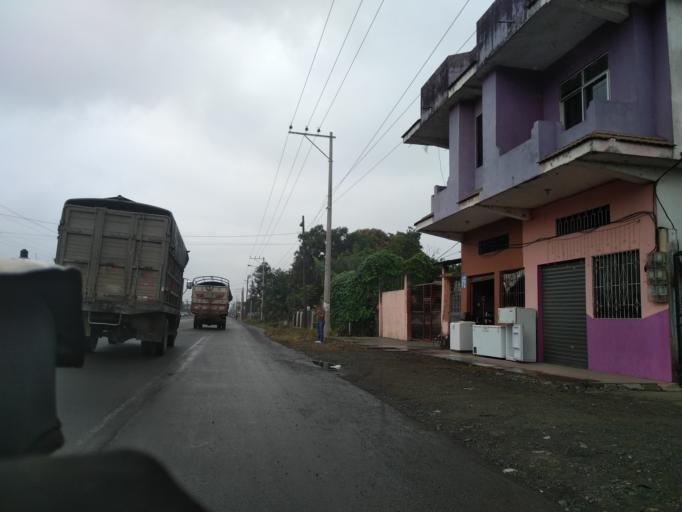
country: EC
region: Cotopaxi
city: La Mana
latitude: -0.9493
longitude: -79.3435
